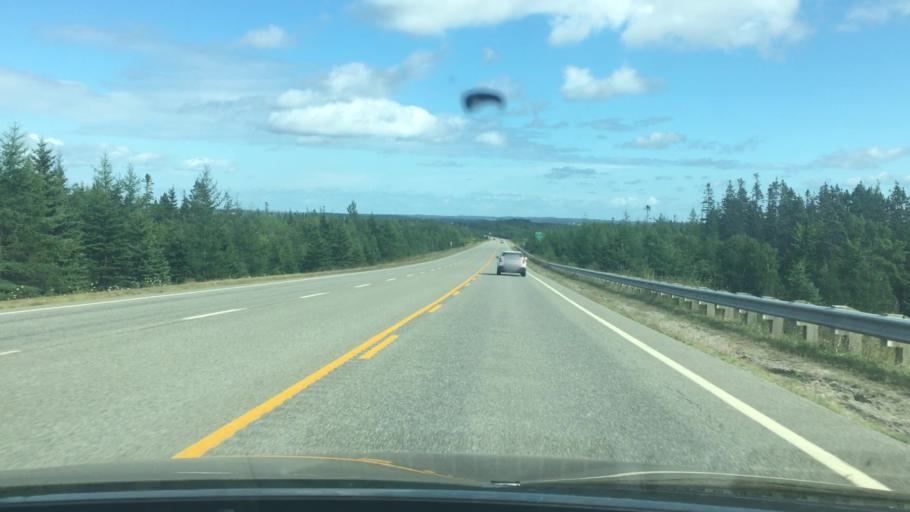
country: CA
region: Nova Scotia
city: Port Hawkesbury
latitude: 45.6196
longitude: -61.1124
